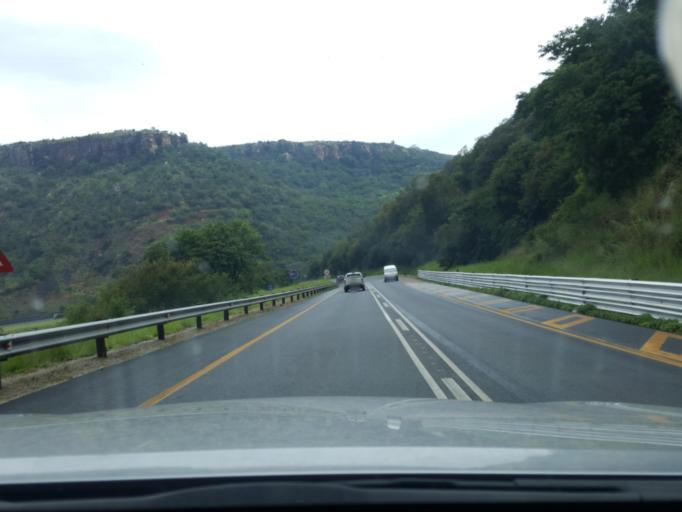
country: ZA
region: Mpumalanga
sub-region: Nkangala District Municipality
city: Belfast
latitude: -25.6401
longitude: 30.3461
